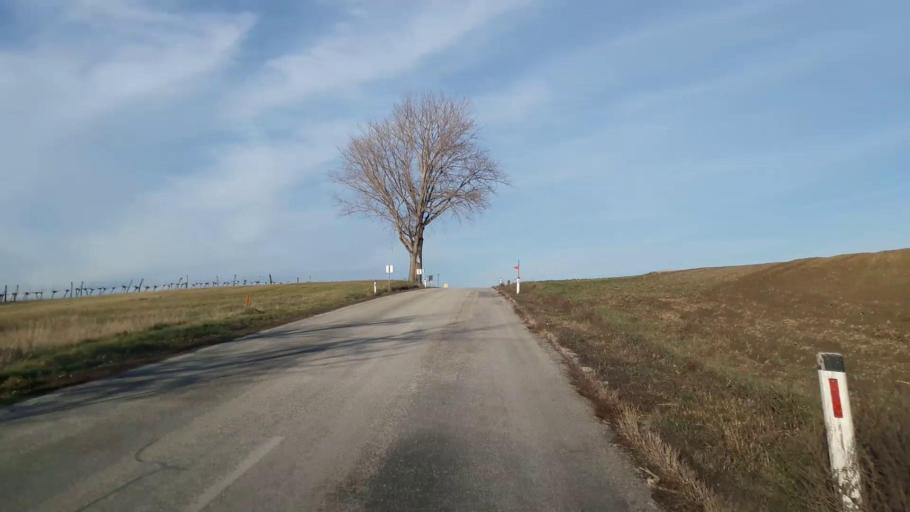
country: AT
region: Lower Austria
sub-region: Politischer Bezirk Ganserndorf
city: Auersthal
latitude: 48.3812
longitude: 16.6299
